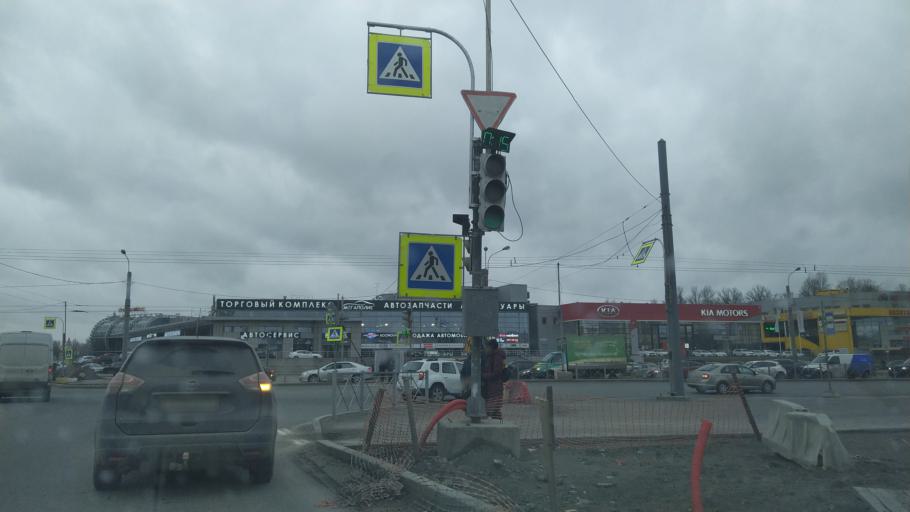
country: RU
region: St.-Petersburg
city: Komendantsky aerodrom
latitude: 59.9997
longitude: 30.2695
